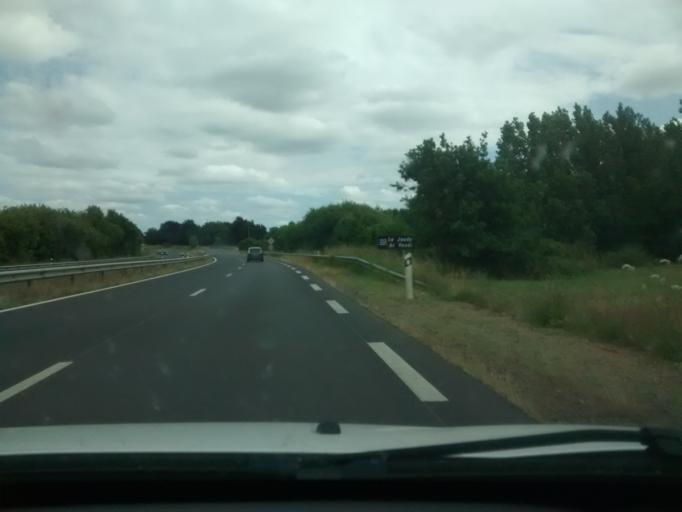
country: FR
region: Brittany
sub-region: Departement des Cotes-d'Armor
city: Pedernec
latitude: 48.5894
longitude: -3.2551
